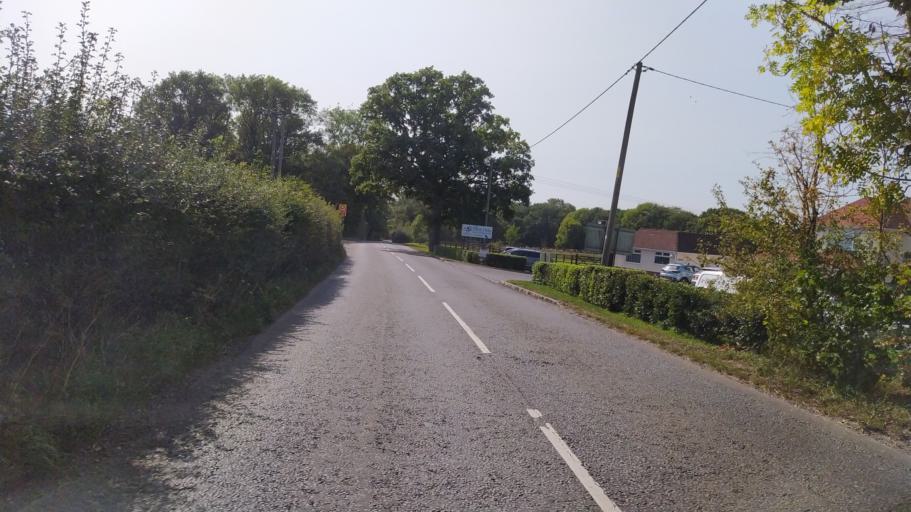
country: GB
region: England
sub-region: Hampshire
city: Bishops Waltham
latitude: 50.9429
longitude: -1.2265
